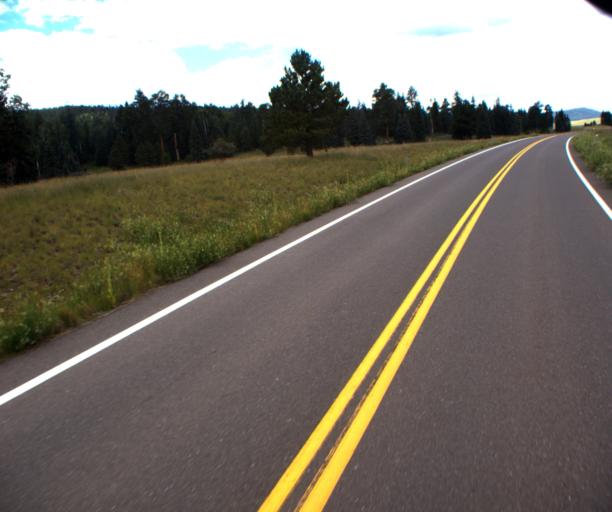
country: US
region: Arizona
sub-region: Apache County
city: Eagar
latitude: 33.9858
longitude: -109.5088
